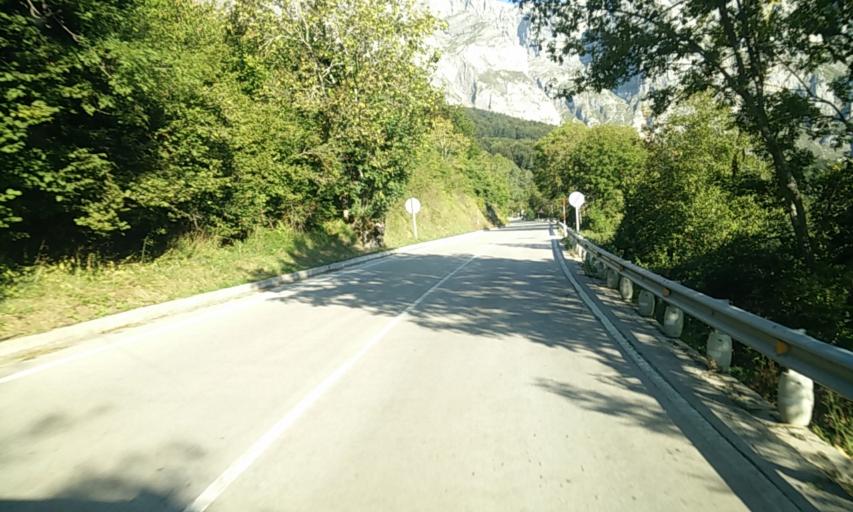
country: ES
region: Castille and Leon
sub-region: Provincia de Leon
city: Posada de Valdeon
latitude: 43.1318
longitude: -4.8081
